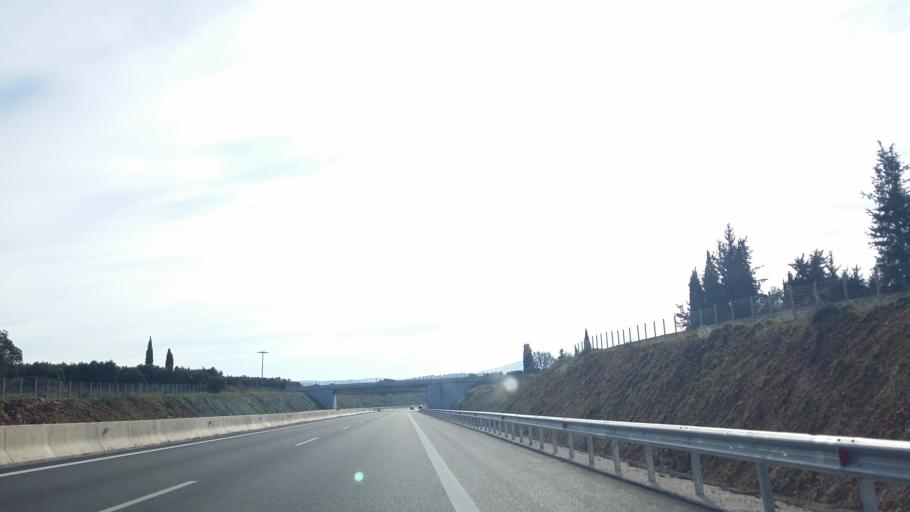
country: GR
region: West Greece
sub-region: Nomos Aitolias kai Akarnanias
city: Sardinia
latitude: 38.8899
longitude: 21.1878
